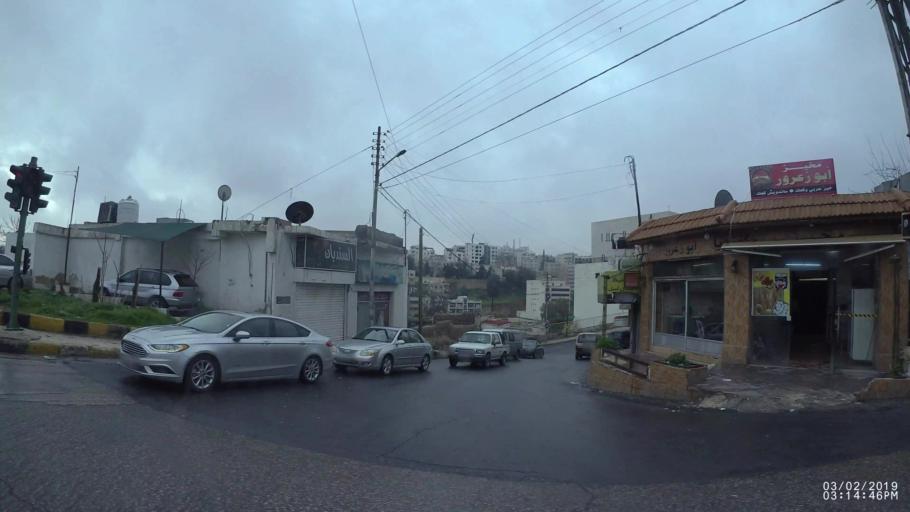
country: JO
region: Amman
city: Amman
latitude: 31.9569
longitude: 35.9326
